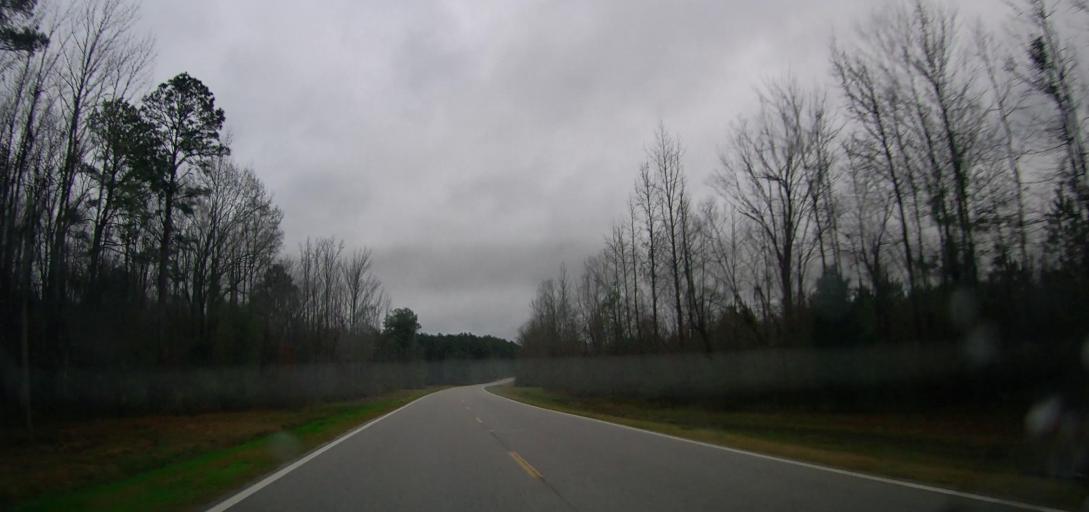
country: US
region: Alabama
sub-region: Bibb County
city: Centreville
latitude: 32.9197
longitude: -87.0320
